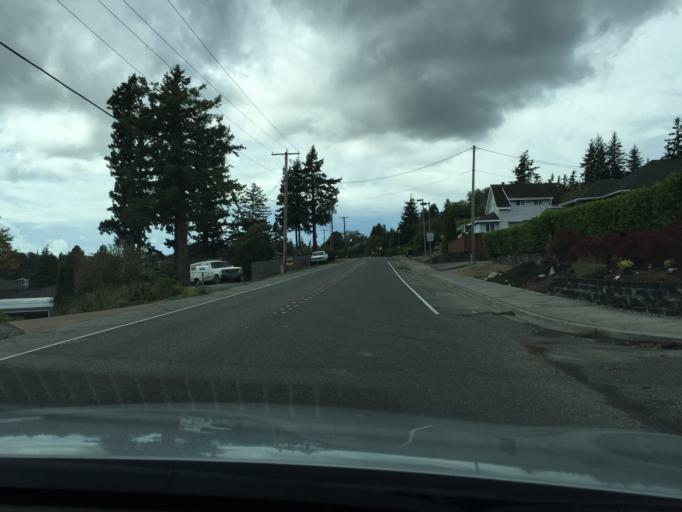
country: US
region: Washington
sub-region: Whatcom County
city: Geneva
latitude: 48.7663
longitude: -122.4134
